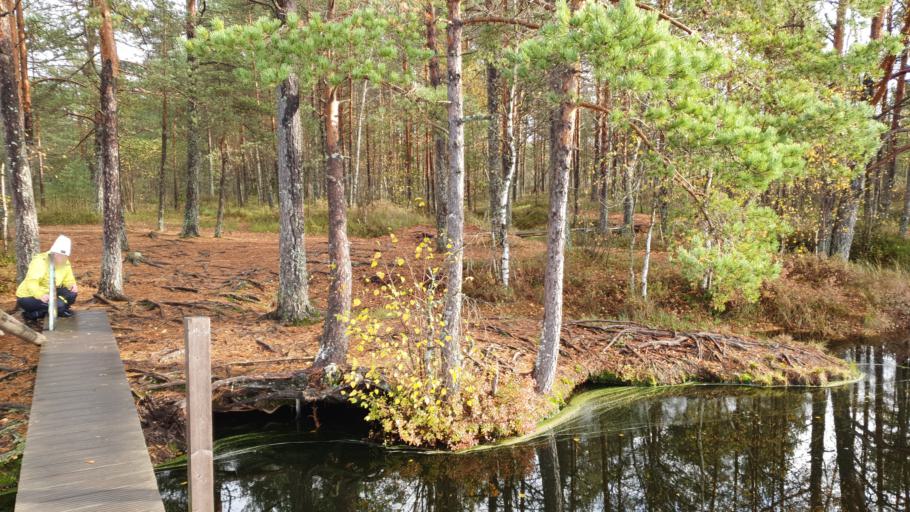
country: EE
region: Raplamaa
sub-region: Kohila vald
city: Kohila
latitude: 59.1149
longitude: 24.7464
